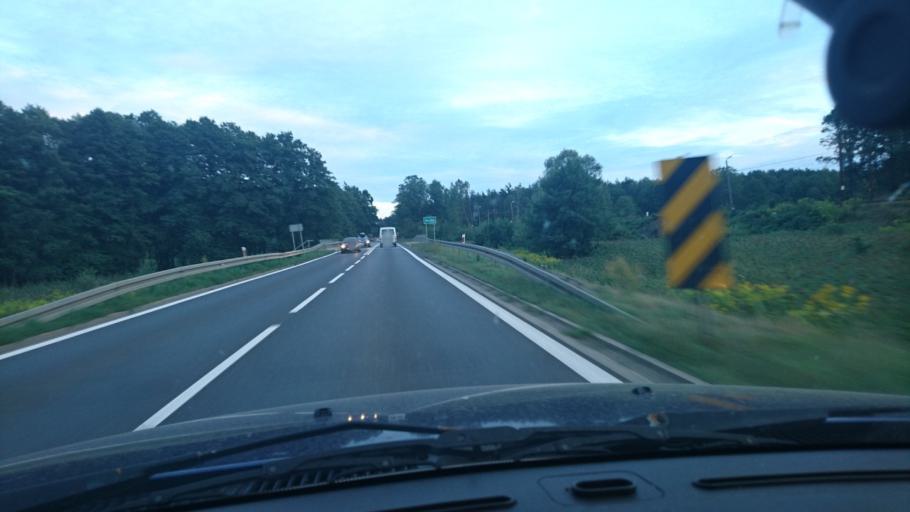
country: PL
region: Silesian Voivodeship
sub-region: Powiat tarnogorski
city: Tworog
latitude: 50.5265
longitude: 18.7186
